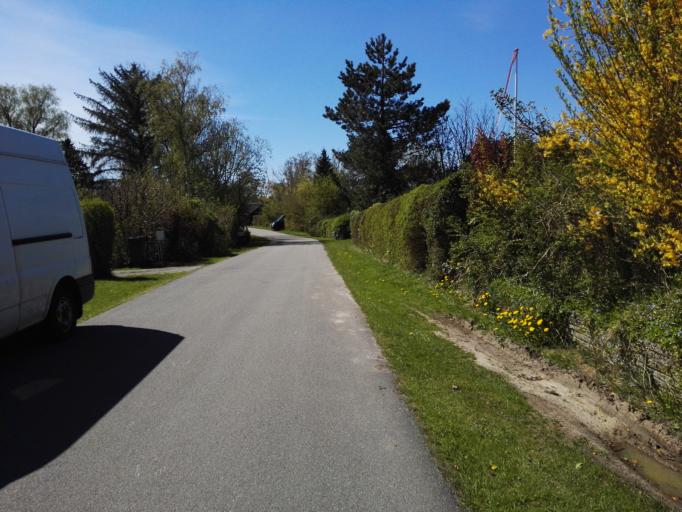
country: DK
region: Capital Region
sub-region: Frederikssund Kommune
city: Frederikssund
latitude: 55.9035
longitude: 12.0560
